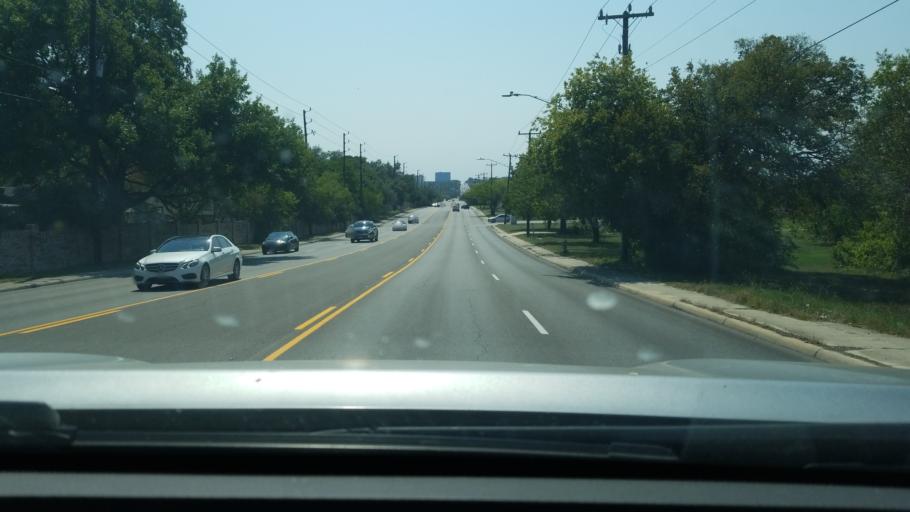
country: US
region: Texas
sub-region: Bexar County
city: Shavano Park
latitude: 29.5633
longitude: -98.5593
